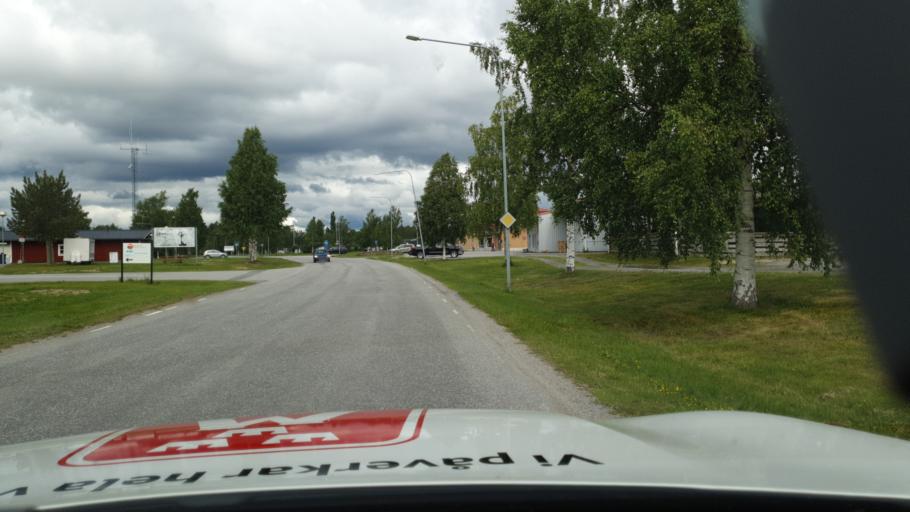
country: SE
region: Vaesterbotten
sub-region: Nordmalings Kommun
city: Nordmaling
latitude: 63.5672
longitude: 19.4959
